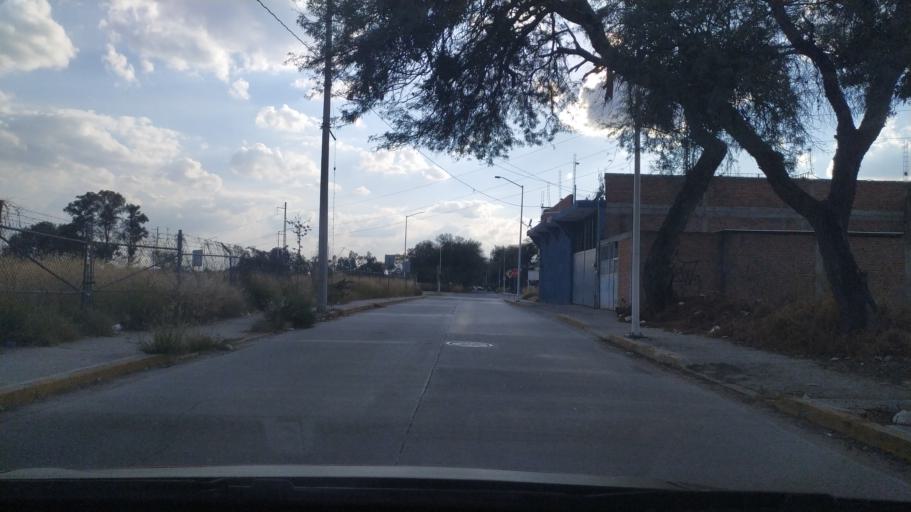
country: MX
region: Guanajuato
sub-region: Purisima del Rincon
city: Monte Grande
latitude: 21.0085
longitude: -101.8695
